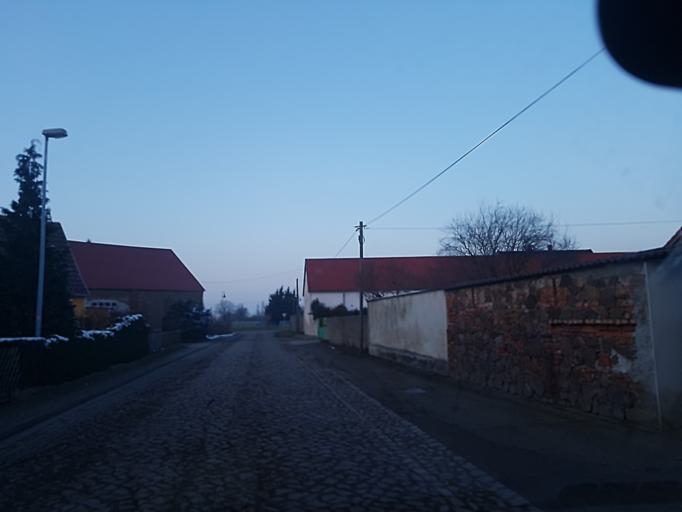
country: DE
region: Brandenburg
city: Muhlberg
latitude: 51.5015
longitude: 13.2819
